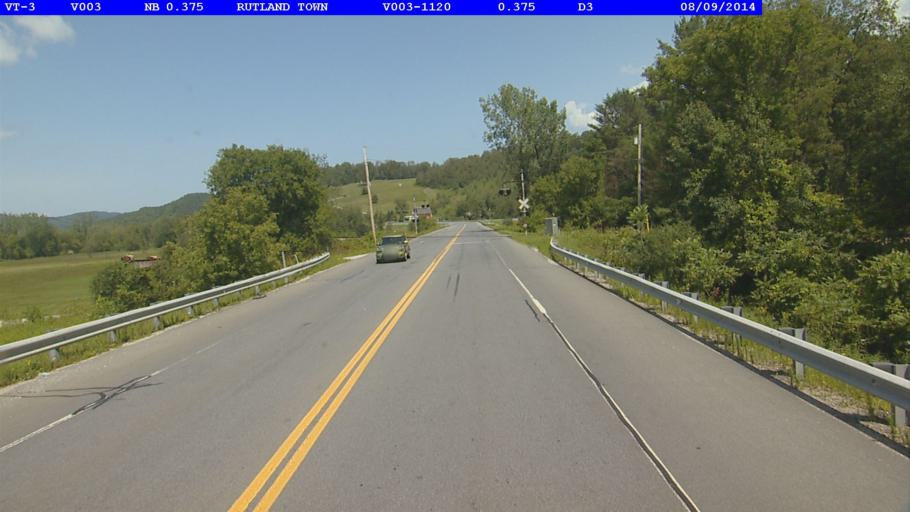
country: US
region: Vermont
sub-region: Rutland County
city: West Rutland
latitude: 43.6092
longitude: -73.0169
